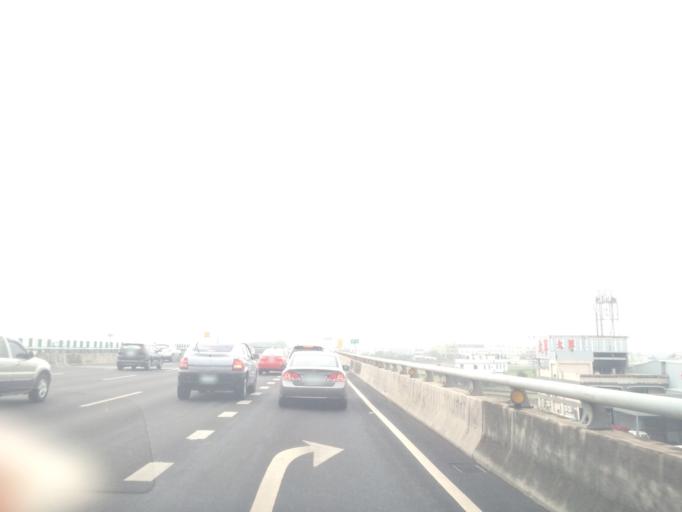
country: TW
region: Taiwan
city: Zhongxing New Village
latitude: 24.0374
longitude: 120.6758
